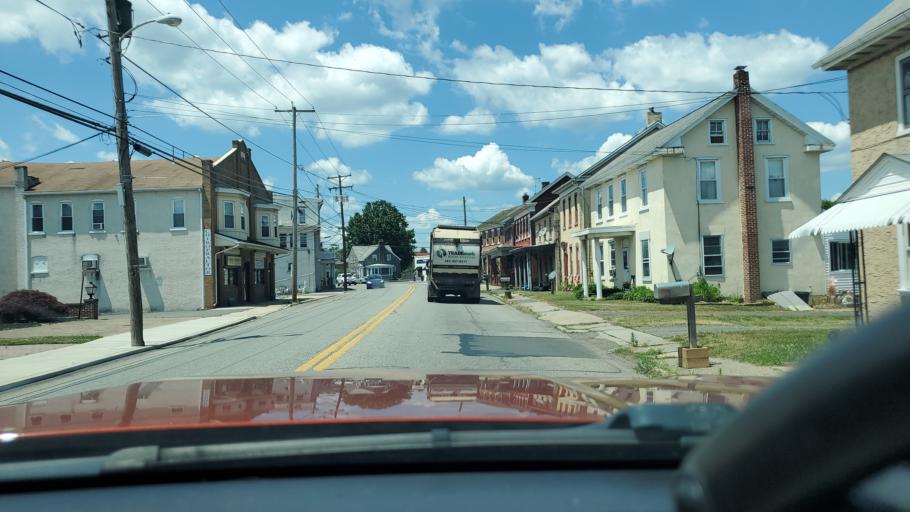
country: US
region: Pennsylvania
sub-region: Montgomery County
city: Gilbertsville
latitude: 40.3202
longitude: -75.6106
